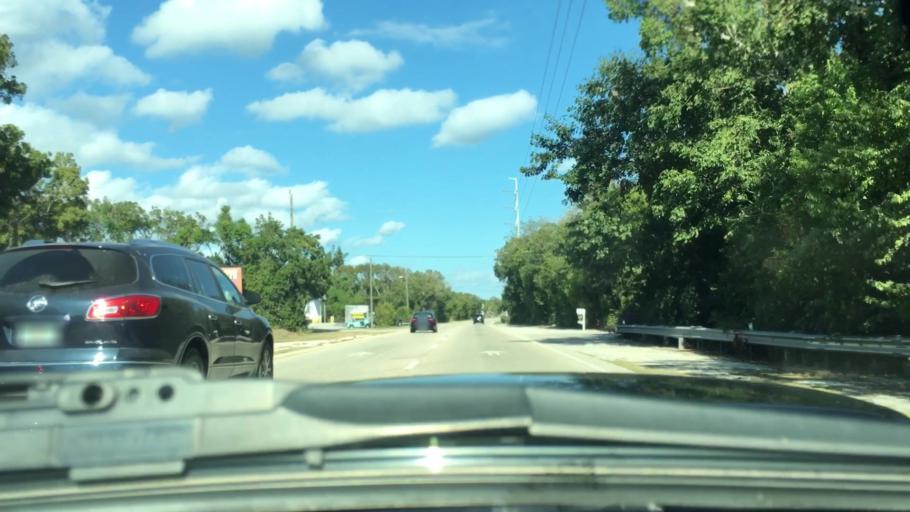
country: US
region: Florida
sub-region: Monroe County
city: Key Largo
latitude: 25.0708
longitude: -80.4659
